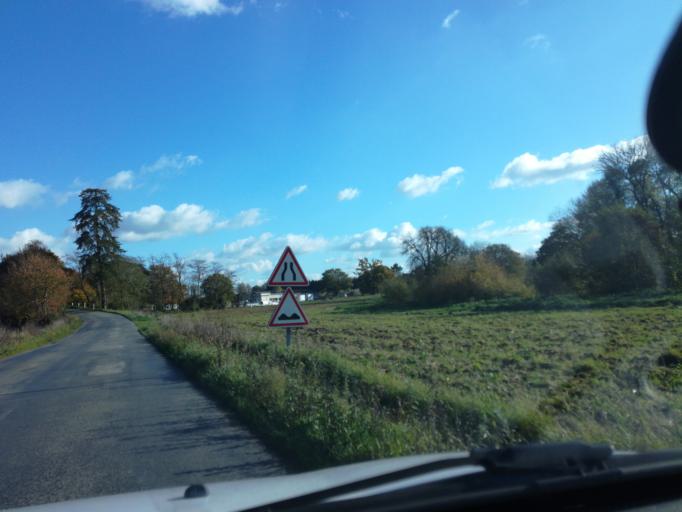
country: FR
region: Brittany
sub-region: Departement d'Ille-et-Vilaine
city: Chavagne
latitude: 48.0294
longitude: -1.7750
